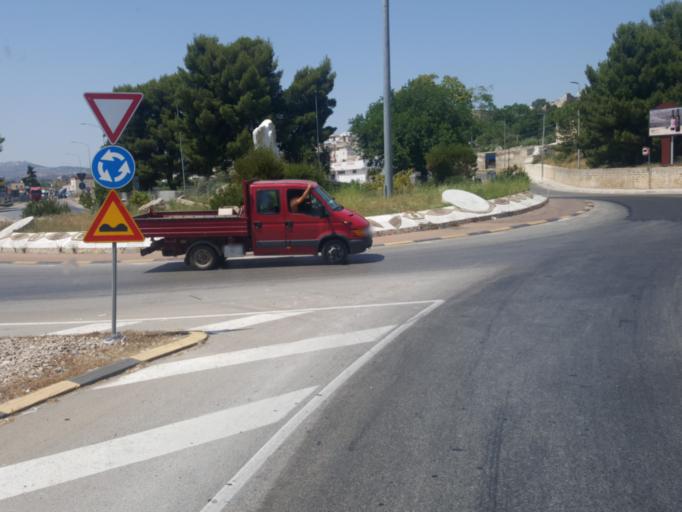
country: IT
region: Apulia
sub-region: Provincia di Taranto
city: Massafra
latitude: 40.5825
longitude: 17.1123
